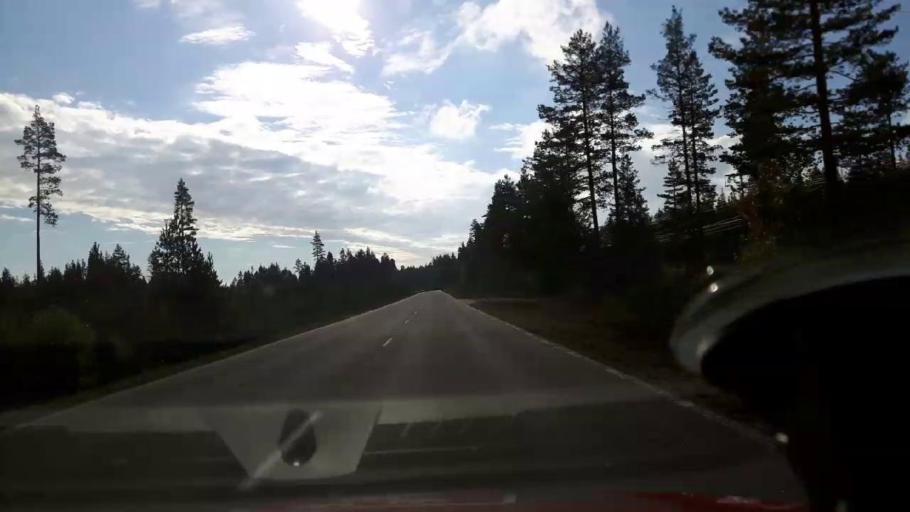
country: SE
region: Vaesternorrland
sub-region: Ange Kommun
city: Ange
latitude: 62.0640
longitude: 15.1107
